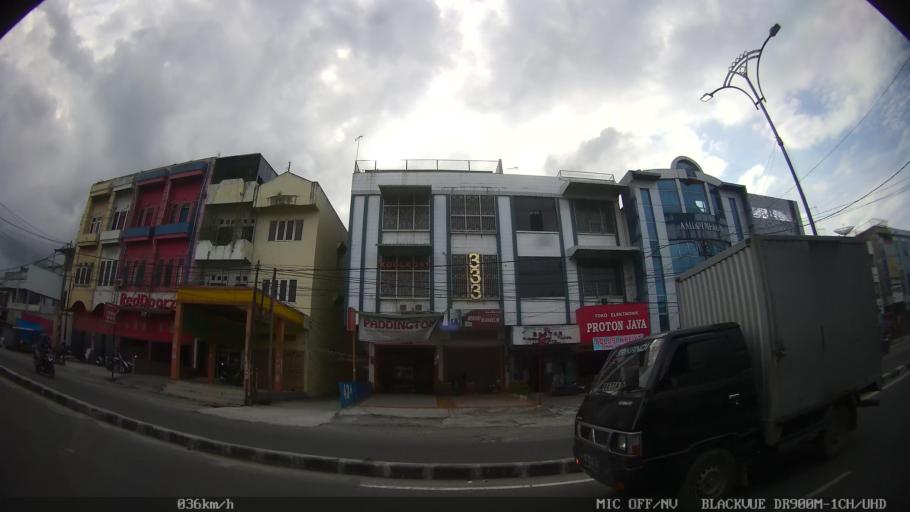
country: ID
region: North Sumatra
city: Medan
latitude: 3.6092
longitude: 98.6742
